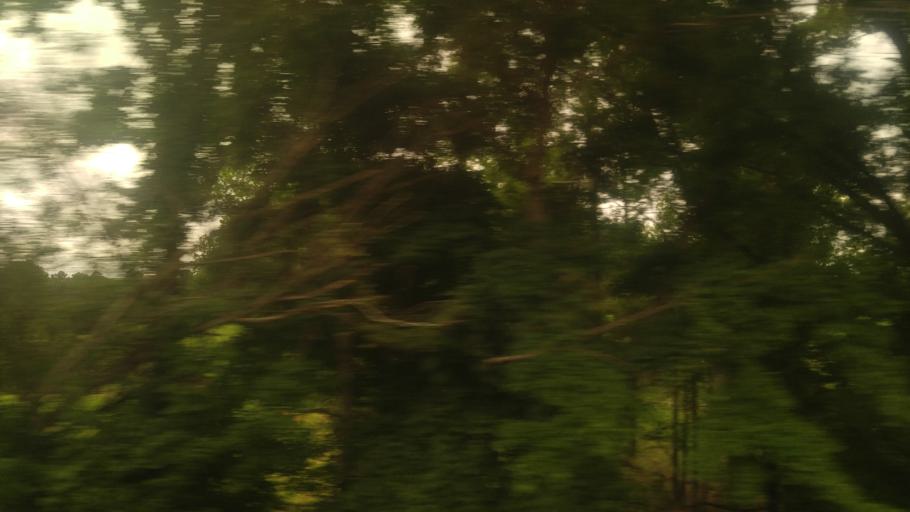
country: US
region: Virginia
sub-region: Hanover County
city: Ashland
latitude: 37.7189
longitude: -77.4937
